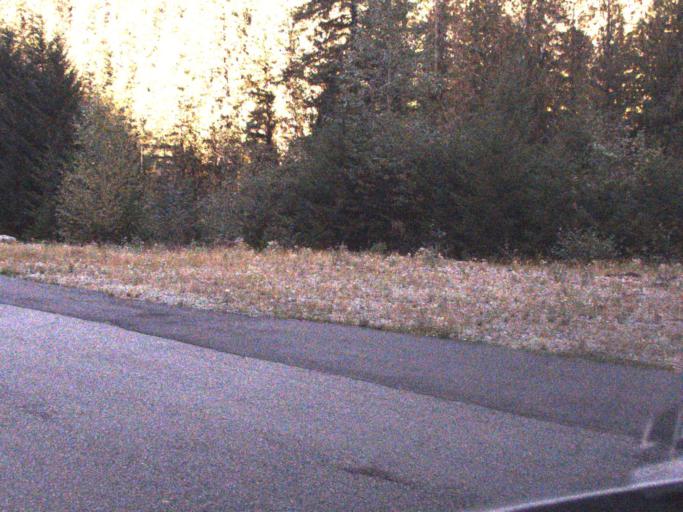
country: US
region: Washington
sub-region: Snohomish County
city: Darrington
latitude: 48.6859
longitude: -120.8860
